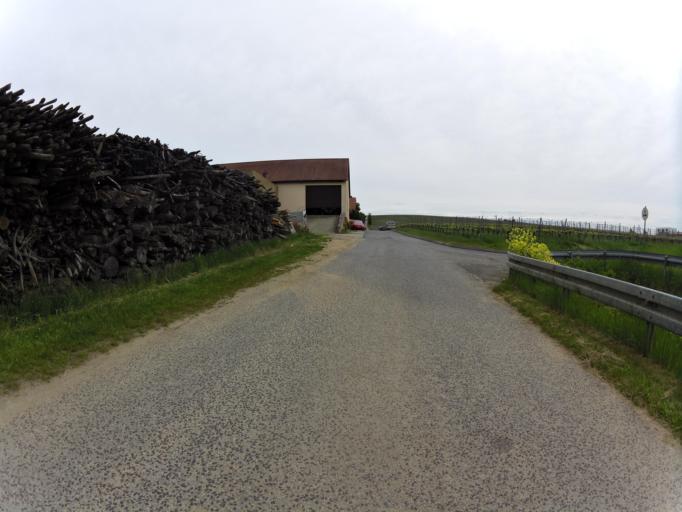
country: DE
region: Bavaria
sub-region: Regierungsbezirk Unterfranken
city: Nordheim
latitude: 49.8563
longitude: 10.1790
